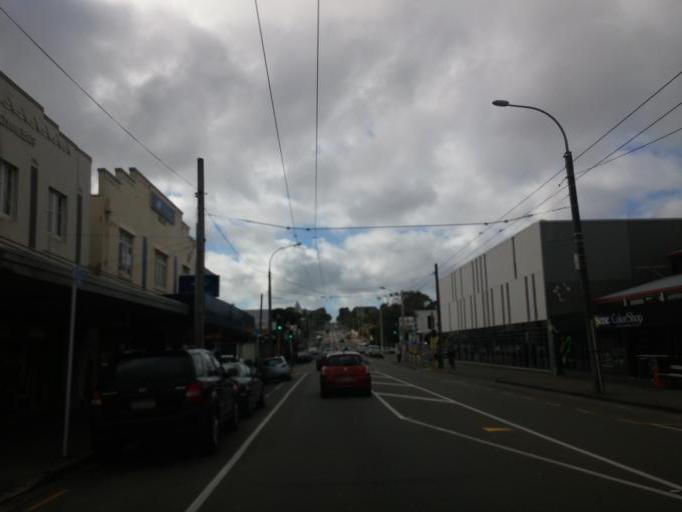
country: NZ
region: Wellington
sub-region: Wellington City
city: Kelburn
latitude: -41.2848
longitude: 174.7369
